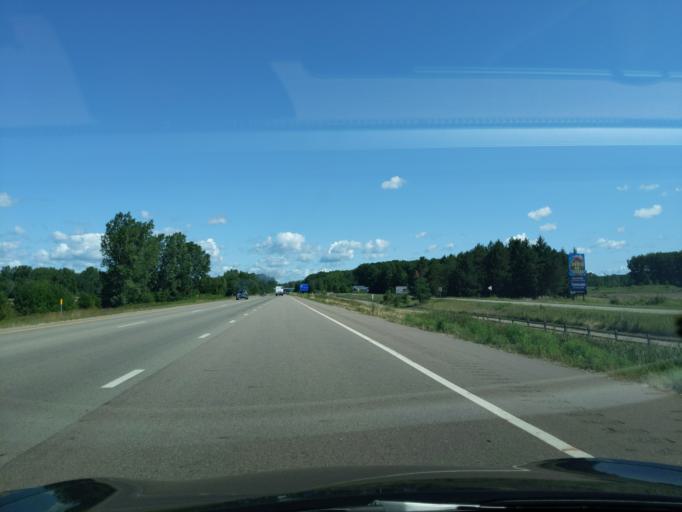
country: US
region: Michigan
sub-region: Gratiot County
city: Saint Louis
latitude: 43.3567
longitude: -84.6010
